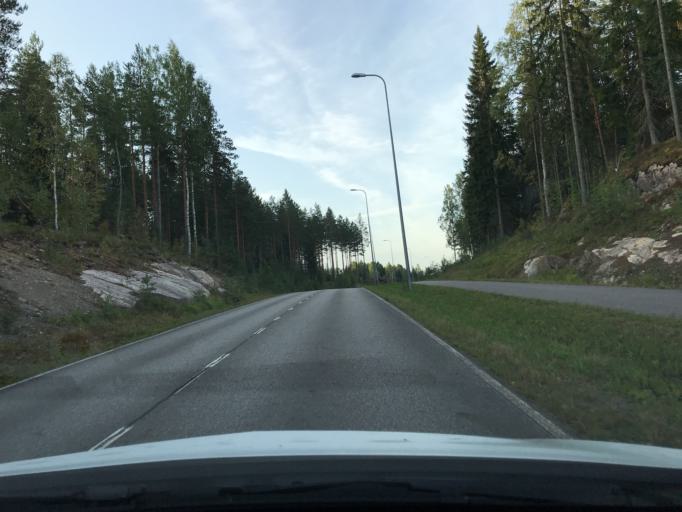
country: FI
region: Uusimaa
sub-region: Helsinki
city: Vihti
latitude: 60.4088
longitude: 24.4734
